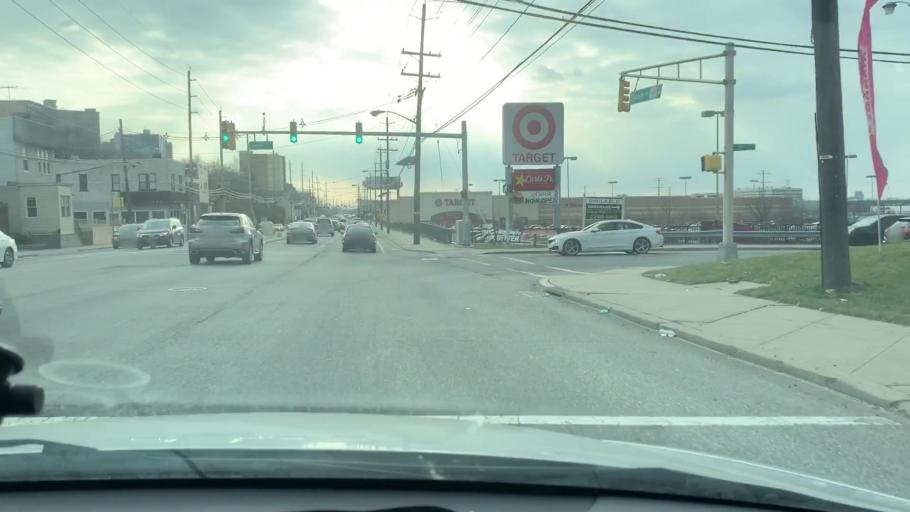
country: US
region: New Jersey
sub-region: Hudson County
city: North Bergen
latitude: 40.8032
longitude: -74.0199
